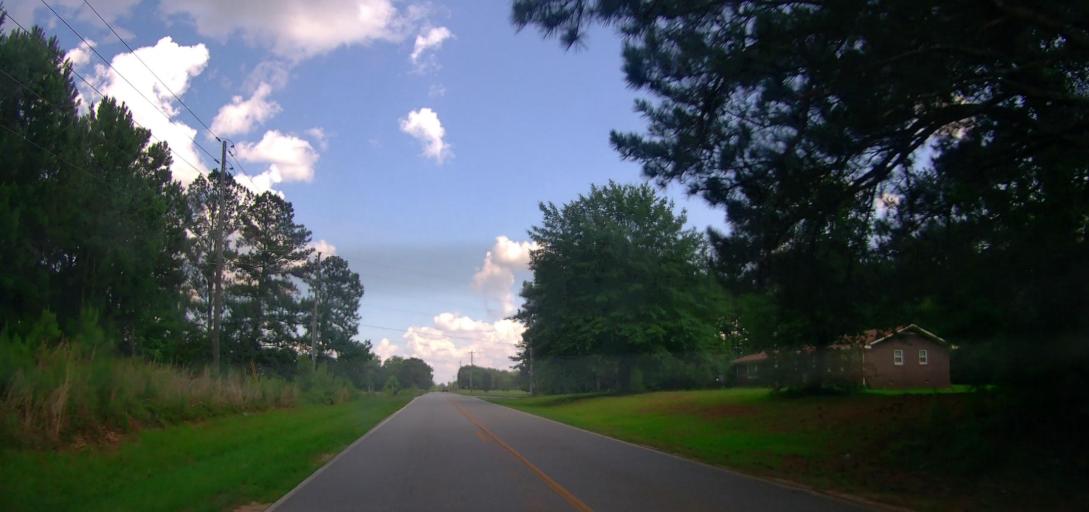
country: US
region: Georgia
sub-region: Butts County
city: Jackson
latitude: 33.2158
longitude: -84.0748
